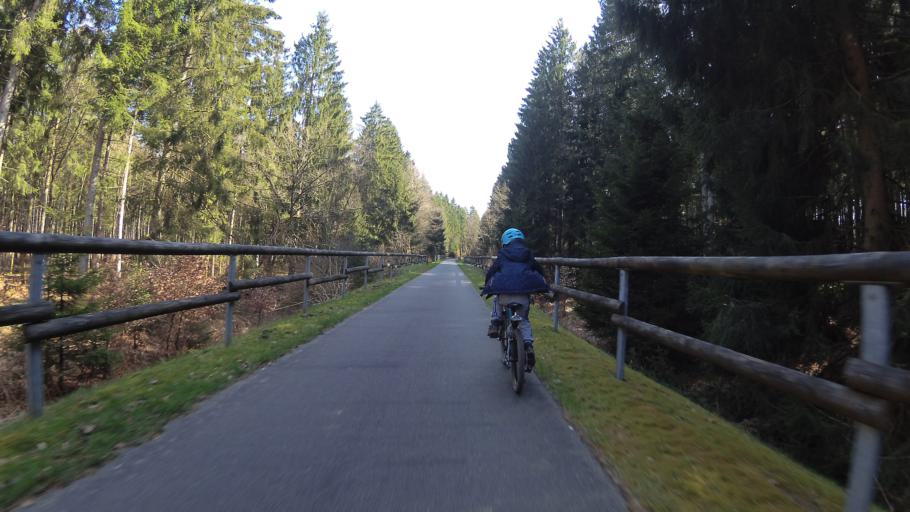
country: DE
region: Rheinland-Pfalz
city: Reinsfeld
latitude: 49.6628
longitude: 6.8540
